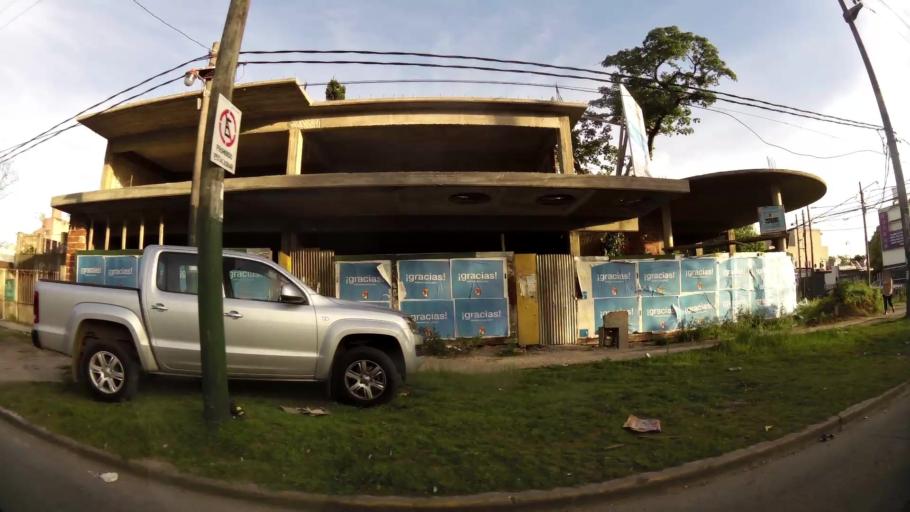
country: AR
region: Buenos Aires
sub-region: Partido de Almirante Brown
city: Adrogue
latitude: -34.7944
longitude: -58.3619
